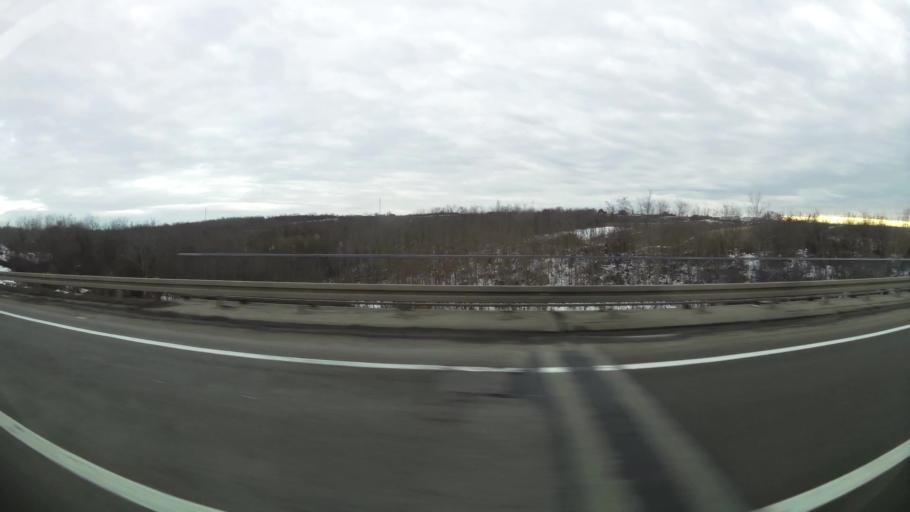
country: RS
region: Central Serbia
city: Sremcica
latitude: 44.7154
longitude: 20.3938
